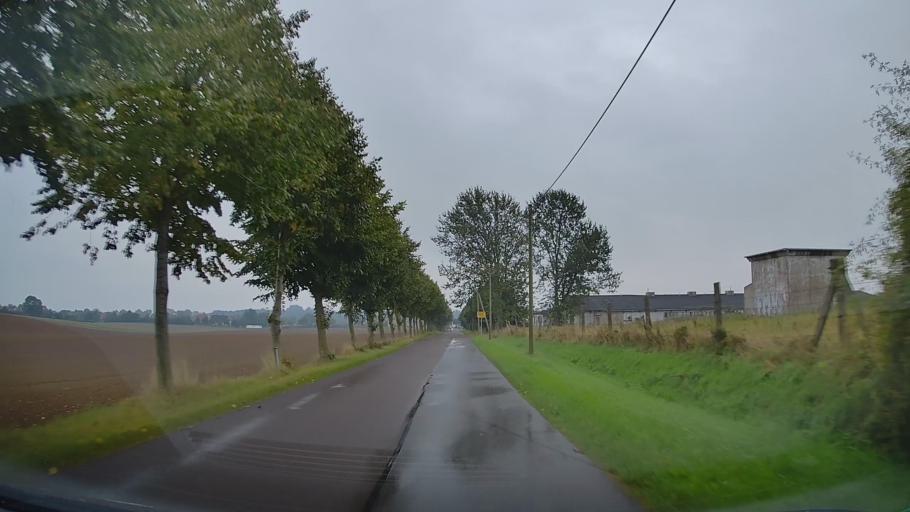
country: DE
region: Mecklenburg-Vorpommern
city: Ostseebad Boltenhagen
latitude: 53.9980
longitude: 11.1803
